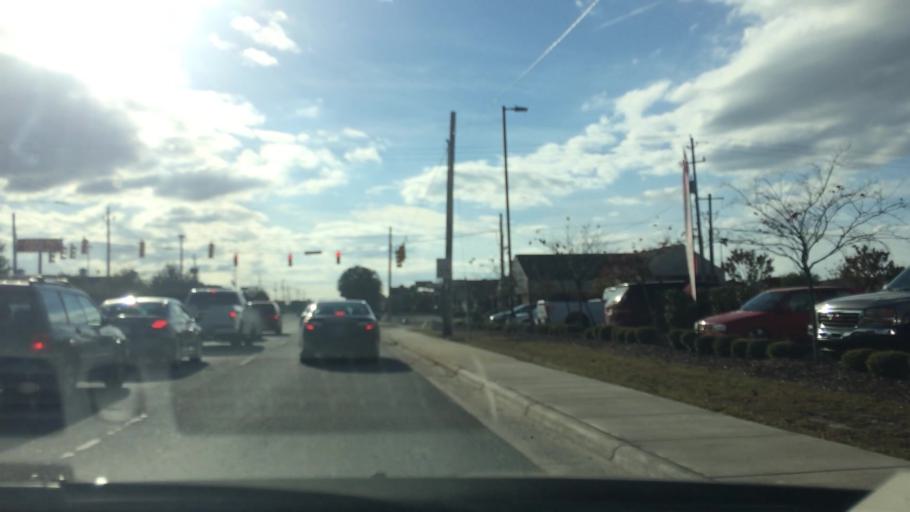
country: US
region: North Carolina
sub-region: Wayne County
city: Elroy
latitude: 35.3747
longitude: -77.9451
